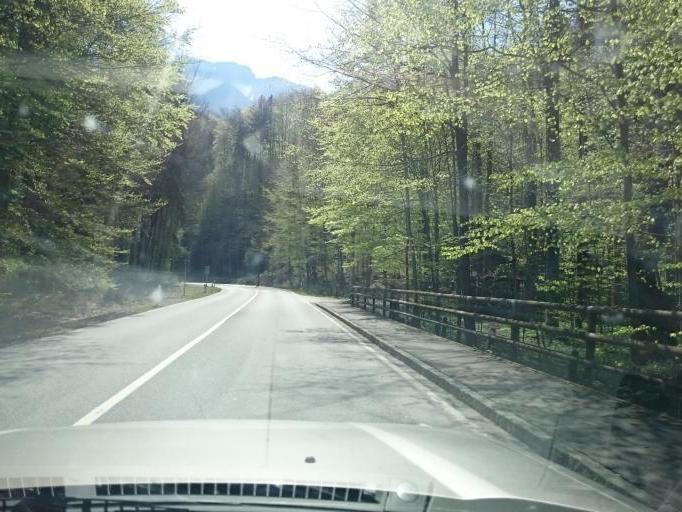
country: DE
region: Bavaria
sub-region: Upper Bavaria
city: Kochel
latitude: 47.6370
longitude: 11.3520
